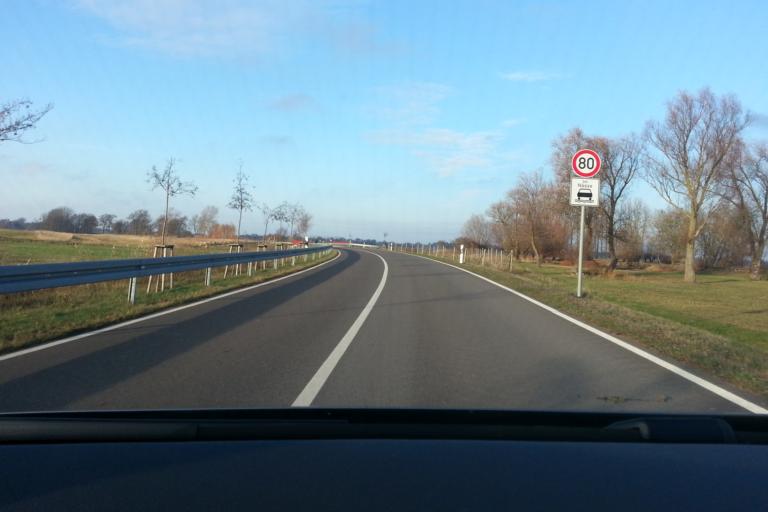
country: DE
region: Mecklenburg-Vorpommern
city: Strasburg
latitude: 53.6227
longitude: 13.7662
